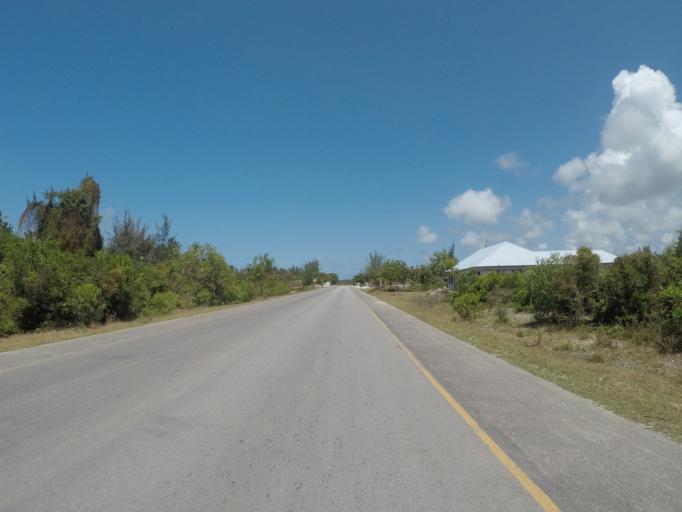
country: TZ
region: Zanzibar Central/South
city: Nganane
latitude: -6.3215
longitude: 39.5443
